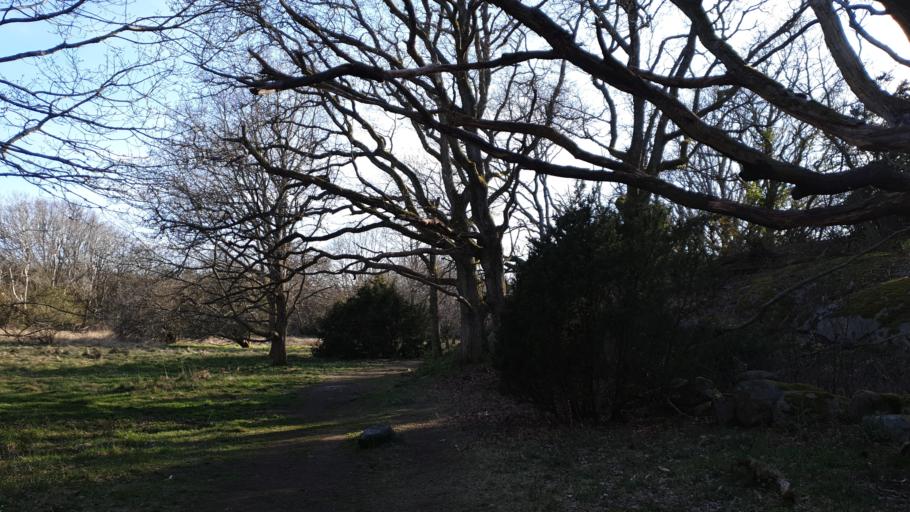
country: SE
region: Vaestra Goetaland
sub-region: Goteborg
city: Billdal
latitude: 57.5899
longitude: 11.9174
